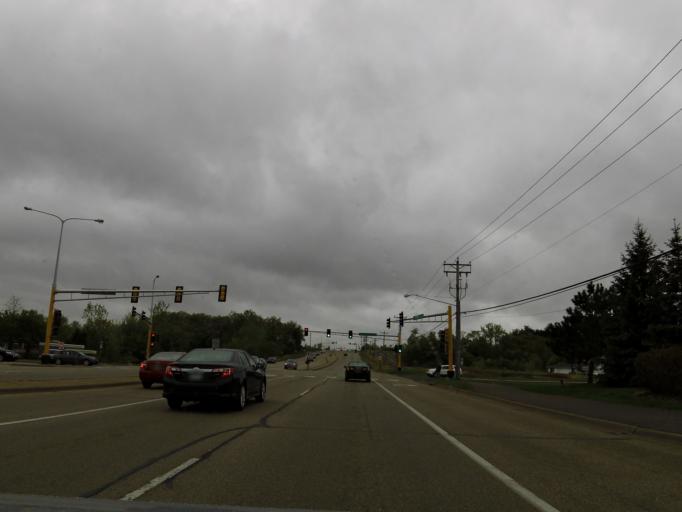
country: US
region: Minnesota
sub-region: Washington County
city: Stillwater
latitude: 45.0403
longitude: -92.8424
